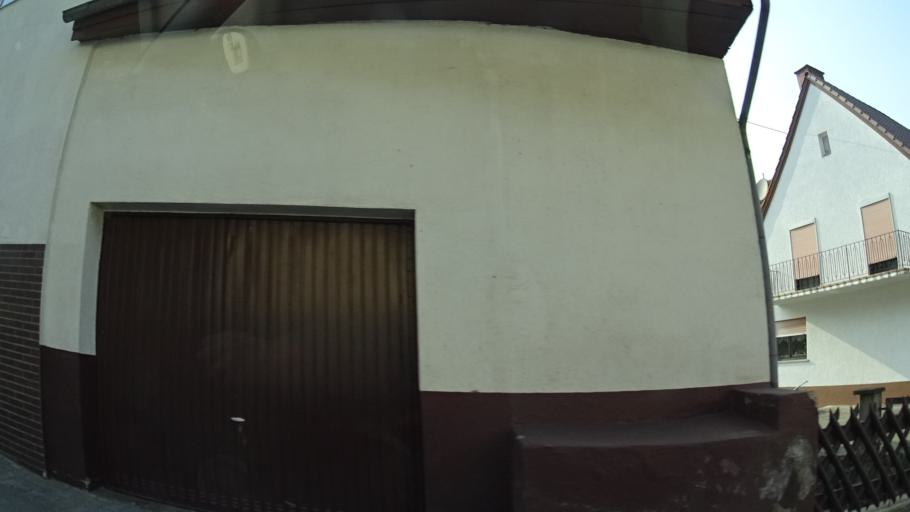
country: DE
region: Rheinland-Pfalz
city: Fockelberg
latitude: 49.5423
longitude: 7.4971
